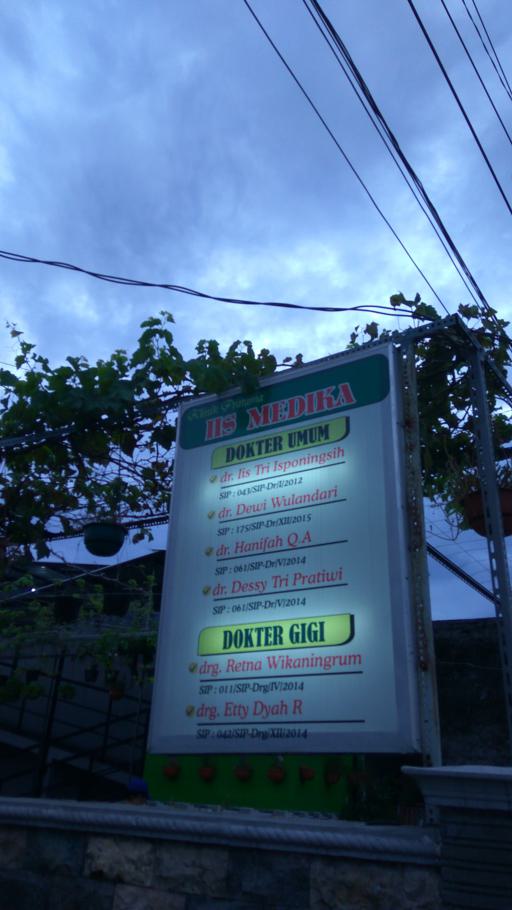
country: ID
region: Central Java
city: Kartasura
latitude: -7.5577
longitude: 110.7460
